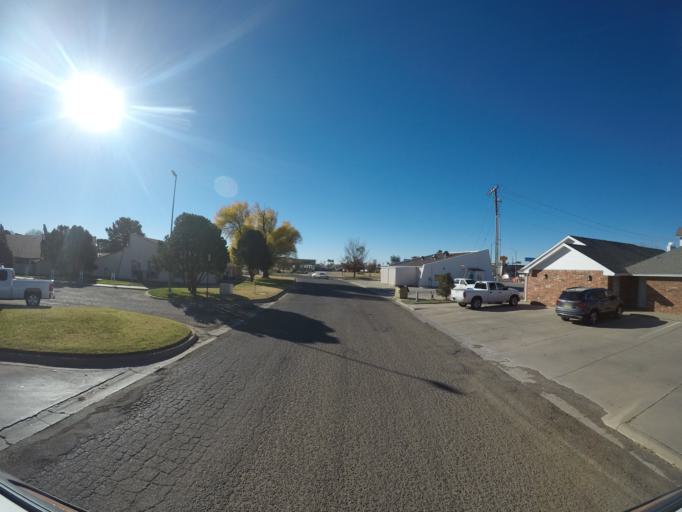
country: US
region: New Mexico
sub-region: Curry County
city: Clovis
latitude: 34.4399
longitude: -103.1957
